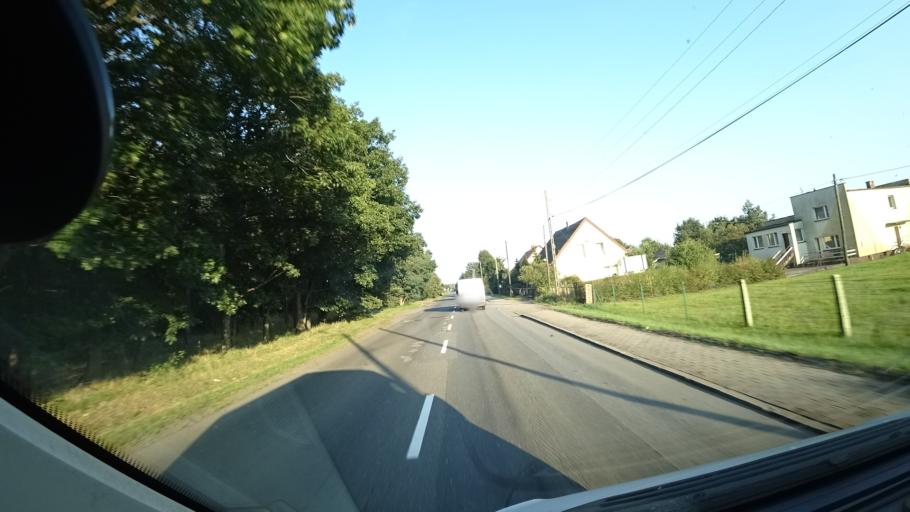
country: PL
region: Opole Voivodeship
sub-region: Powiat kedzierzynsko-kozielski
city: Dziergowice
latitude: 50.2824
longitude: 18.3186
